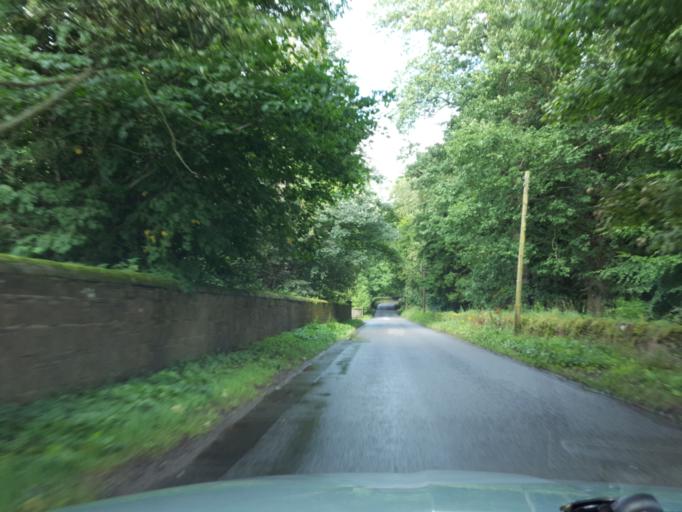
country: GB
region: Scotland
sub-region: Aberdeenshire
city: Laurencekirk
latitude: 56.8578
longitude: -2.5729
